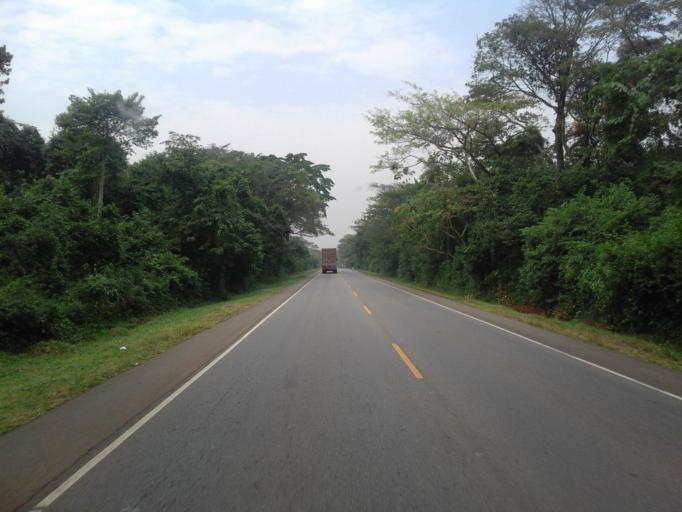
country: UG
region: Eastern Region
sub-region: Busia District
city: Busia
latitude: 0.5317
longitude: 33.9867
